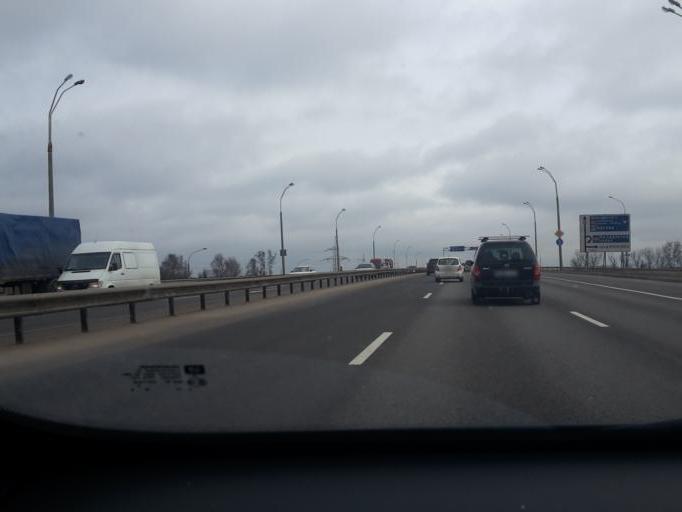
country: BY
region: Minsk
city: Zhdanovichy
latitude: 53.9406
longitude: 27.4322
